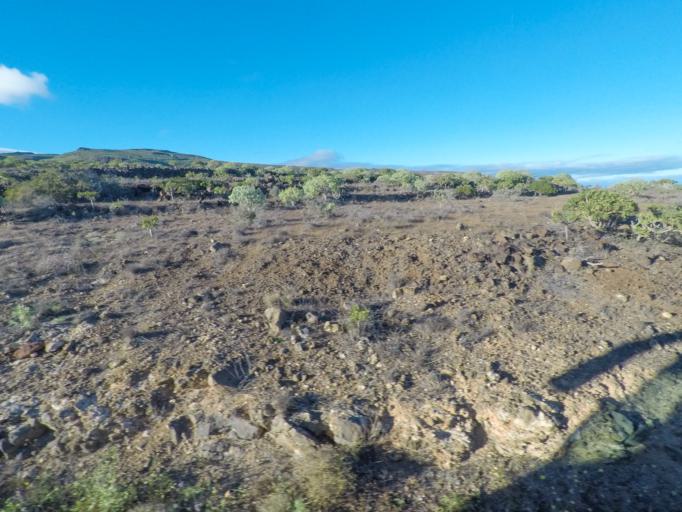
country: ES
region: Canary Islands
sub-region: Provincia de Santa Cruz de Tenerife
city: San Sebastian de la Gomera
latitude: 28.0825
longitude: -17.1376
